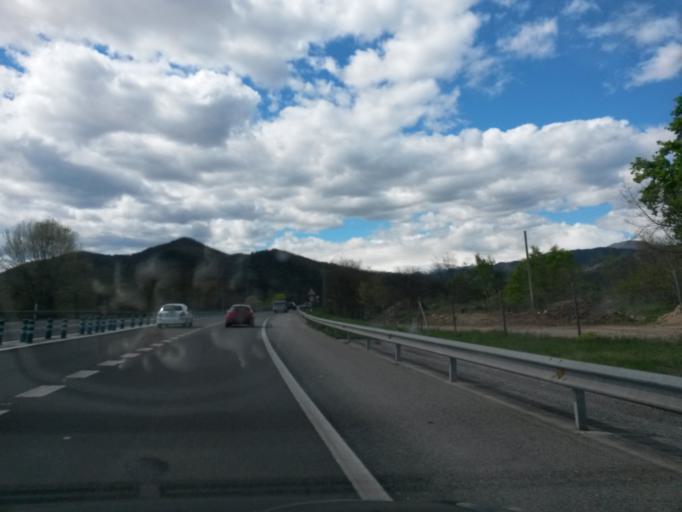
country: ES
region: Catalonia
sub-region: Provincia de Girona
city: MeteOlot
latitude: 42.1952
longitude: 2.5025
